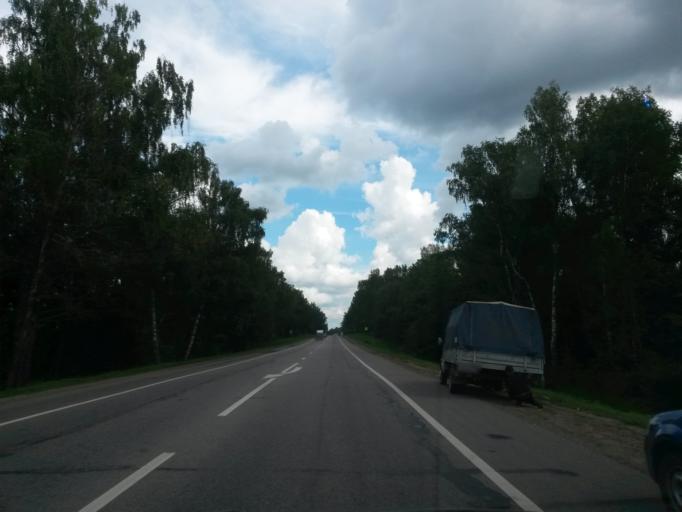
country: RU
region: Vladimir
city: Strunino
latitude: 56.5857
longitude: 38.6094
